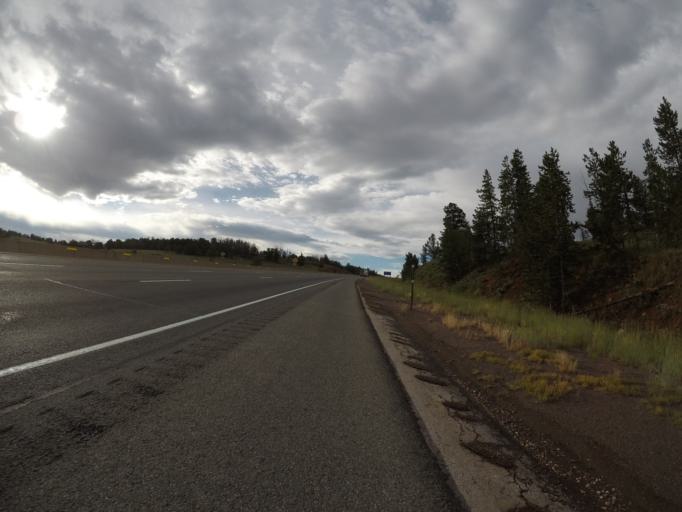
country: US
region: Wyoming
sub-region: Albany County
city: Laramie
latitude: 41.2542
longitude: -105.4473
